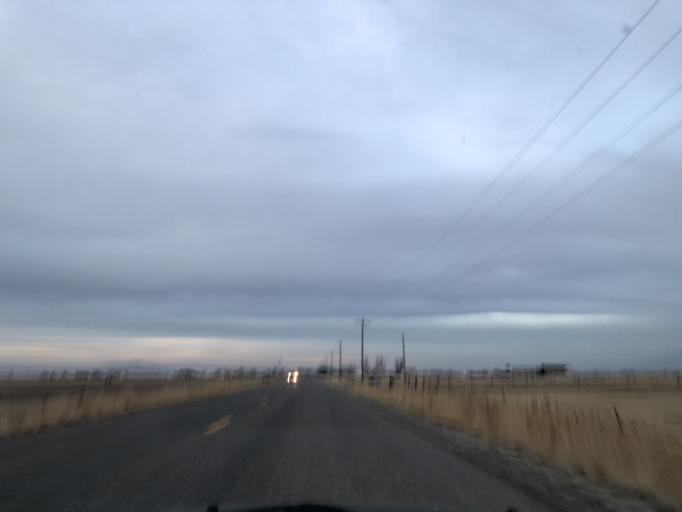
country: US
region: Utah
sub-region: Cache County
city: Benson
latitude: 41.7731
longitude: -111.9117
